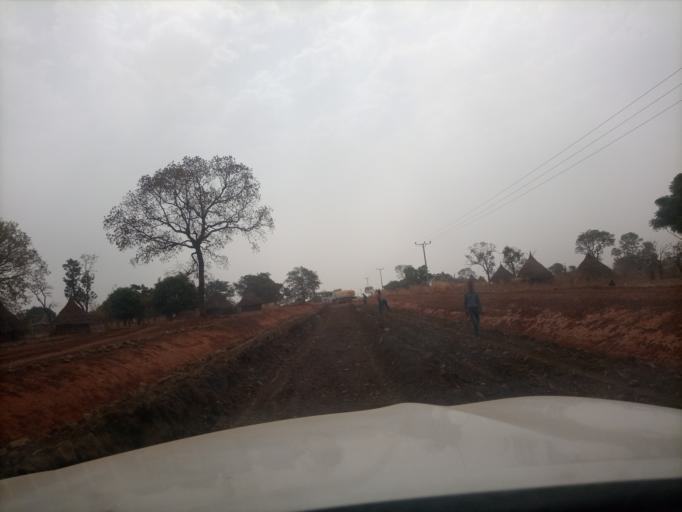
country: ET
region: Oromiya
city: Mendi
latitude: 10.1278
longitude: 35.1322
